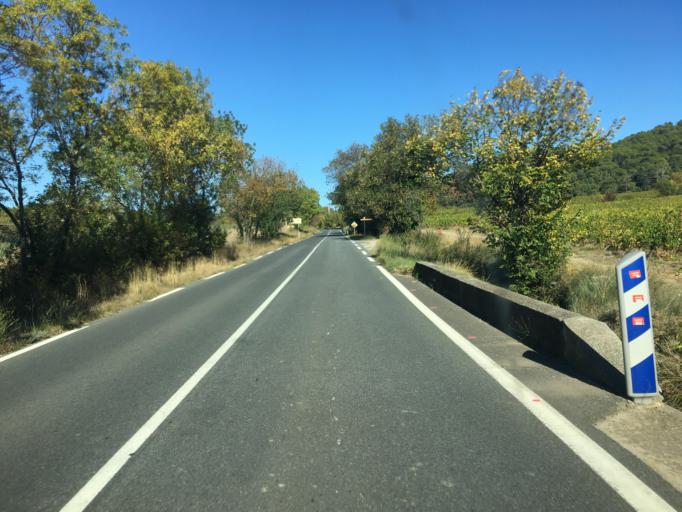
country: FR
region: Languedoc-Roussillon
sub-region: Departement de l'Herault
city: Nebian
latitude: 43.6121
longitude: 3.4052
